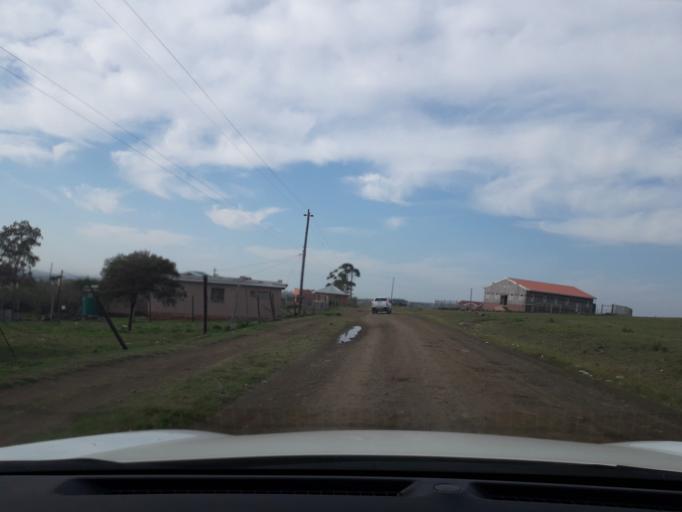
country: ZA
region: Eastern Cape
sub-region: Buffalo City Metropolitan Municipality
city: Bhisho
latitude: -32.9340
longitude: 27.3794
